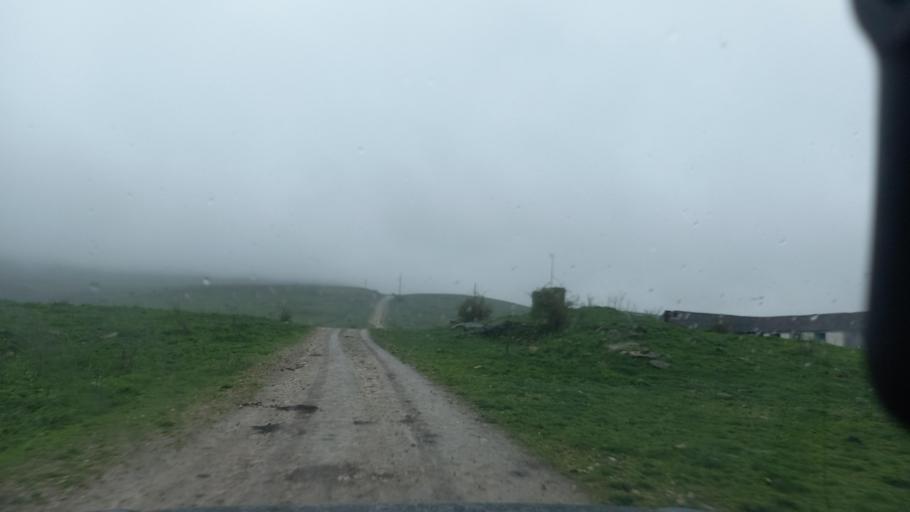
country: RU
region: Kabardino-Balkariya
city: Kamennomostskoye
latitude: 43.6812
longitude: 42.9864
